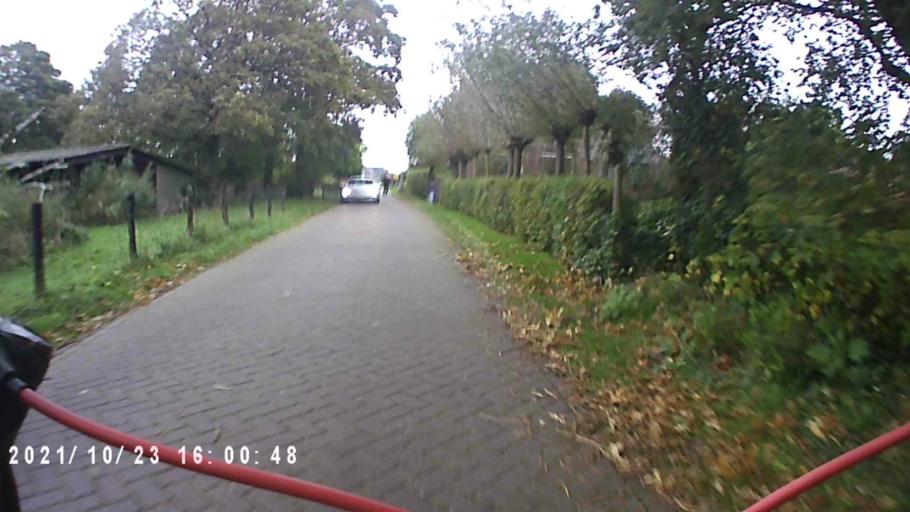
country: NL
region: North Holland
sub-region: Gemeente Langedijk
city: Broek op Langedijk
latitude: 52.6479
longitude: 4.7817
